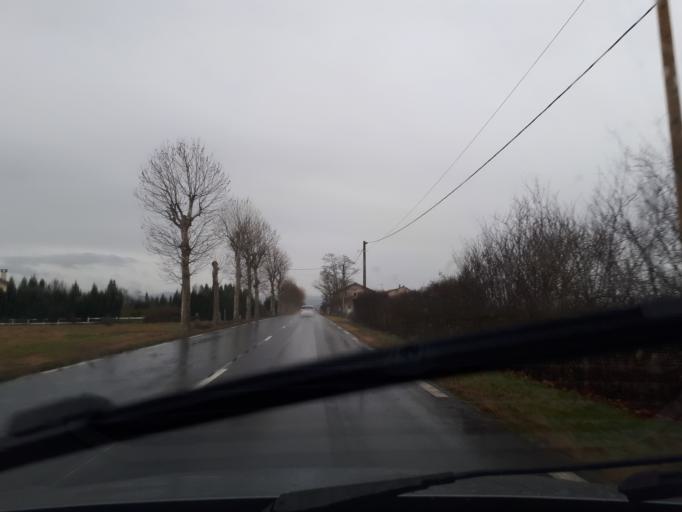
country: FR
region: Rhone-Alpes
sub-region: Departement de la Loire
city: Boen-sur-Lignon
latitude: 45.7381
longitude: 4.1097
